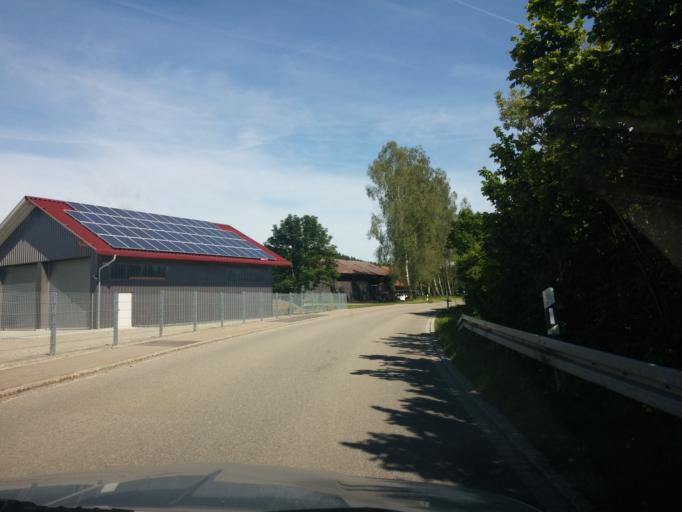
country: DE
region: Bavaria
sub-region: Swabia
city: Lautrach
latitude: 47.9007
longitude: 10.1328
